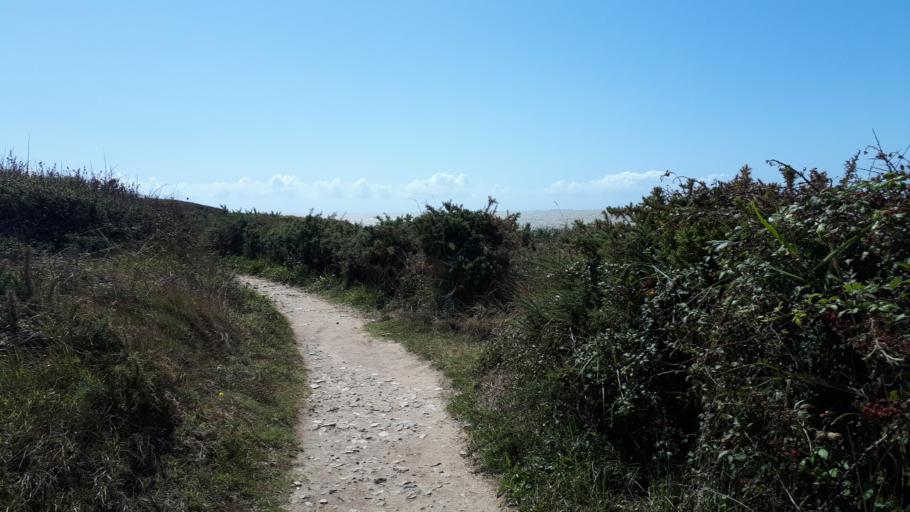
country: FR
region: Brittany
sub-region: Departement du Morbihan
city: Penestin
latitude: 47.4894
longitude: -2.5009
